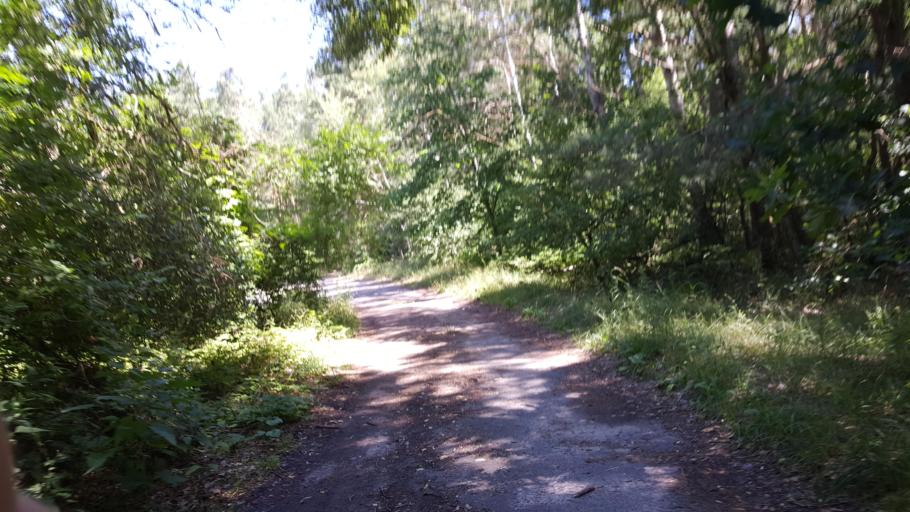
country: BY
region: Brest
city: Kamyanyets
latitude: 52.3267
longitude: 23.8997
